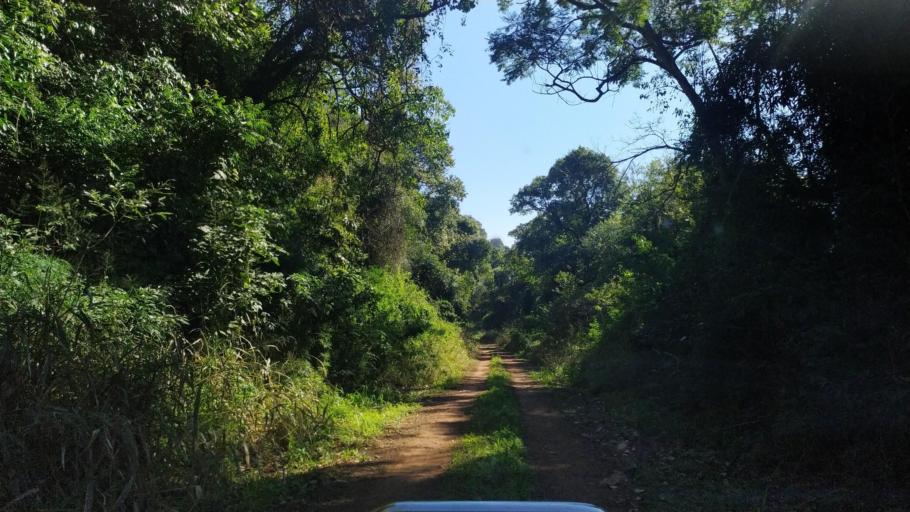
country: AR
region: Misiones
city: El Alcazar
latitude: -26.7598
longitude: -54.5792
